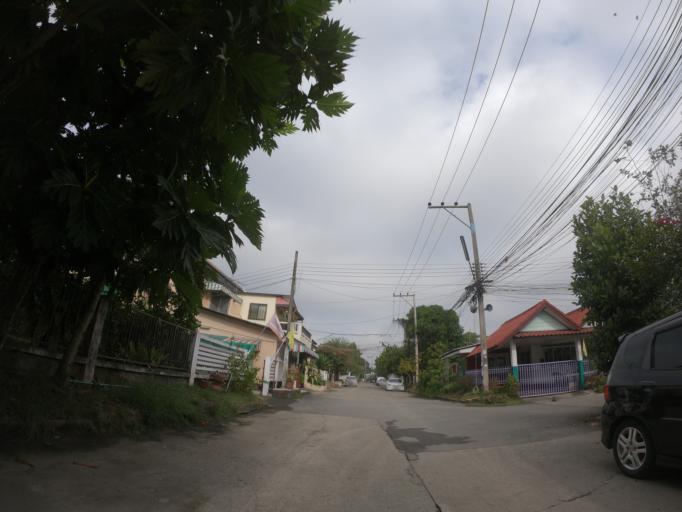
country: TH
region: Chiang Mai
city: Chiang Mai
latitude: 18.7594
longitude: 98.9770
